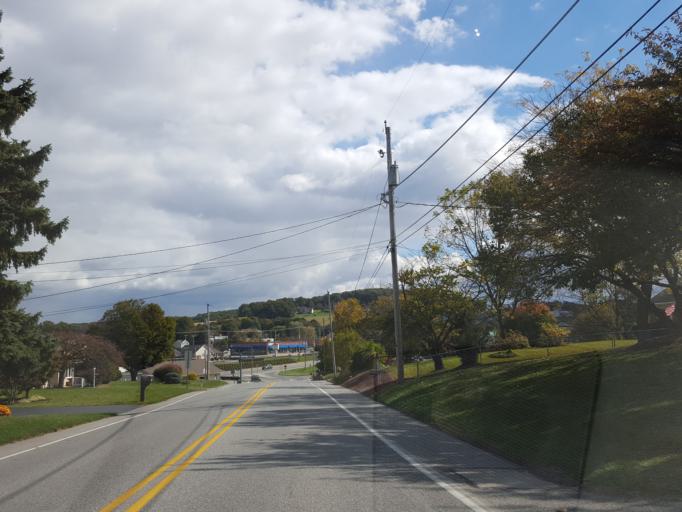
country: US
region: Pennsylvania
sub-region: York County
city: Yoe
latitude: 39.9194
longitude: -76.6341
